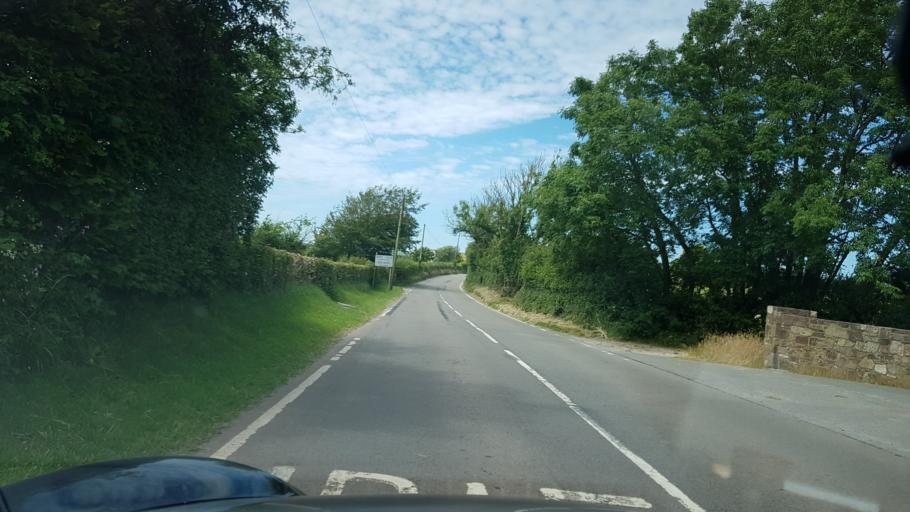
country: GB
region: Wales
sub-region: Carmarthenshire
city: Whitland
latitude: 51.7722
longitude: -4.5970
